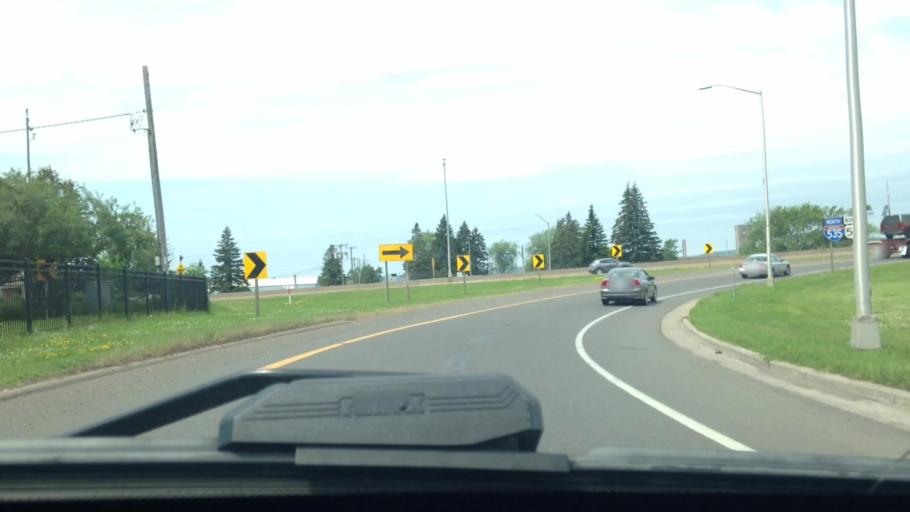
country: US
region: Wisconsin
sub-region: Douglas County
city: Superior
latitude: 46.7340
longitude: -92.0965
